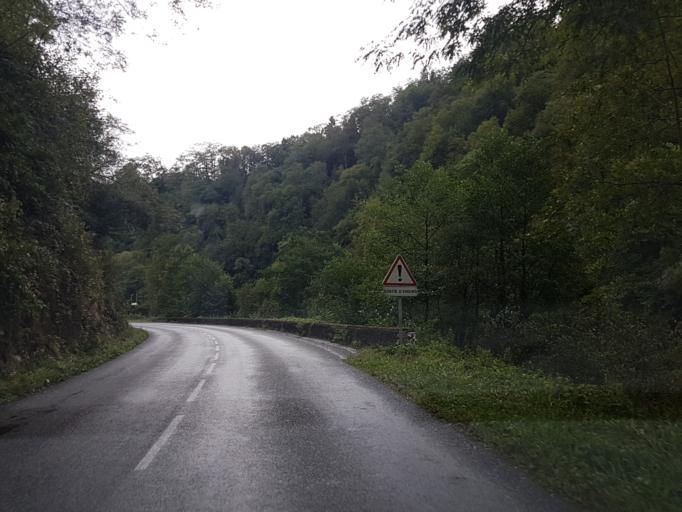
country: FR
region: Midi-Pyrenees
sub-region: Departement de l'Ariege
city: Saint-Girons
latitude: 42.9061
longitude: 1.2123
